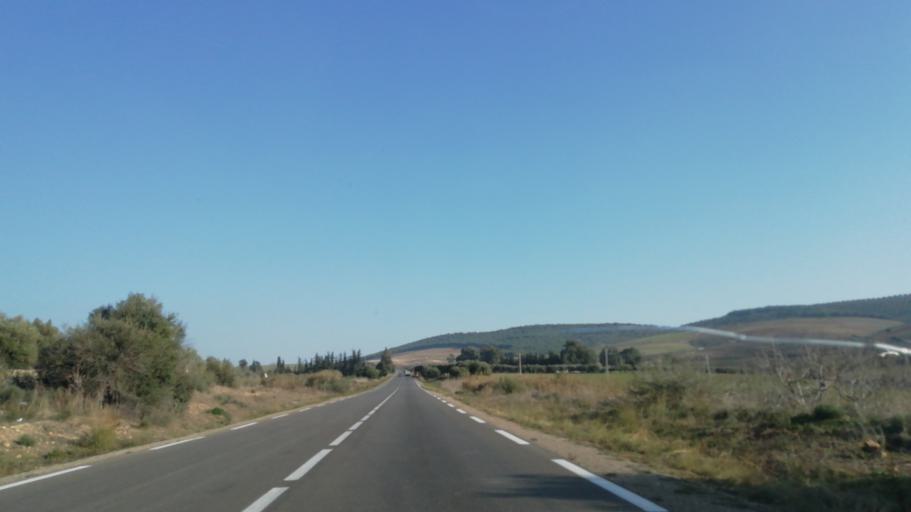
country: DZ
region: Ain Temouchent
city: Hammam Bou Hadjar
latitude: 35.1691
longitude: -0.9009
